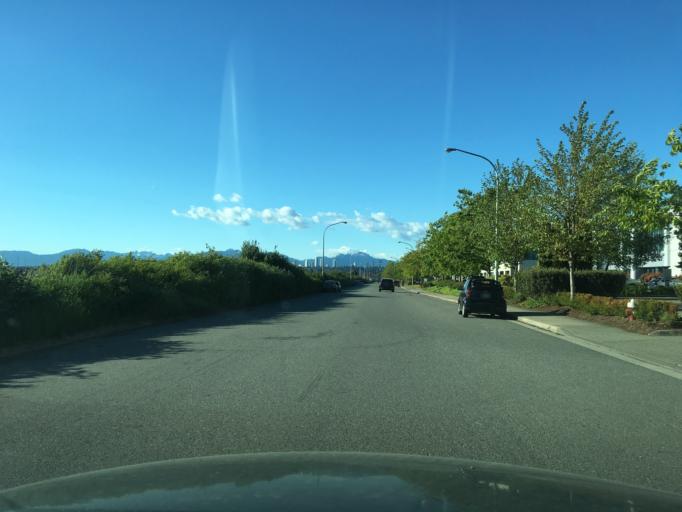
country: CA
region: British Columbia
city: Delta
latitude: 49.1643
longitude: -122.9939
